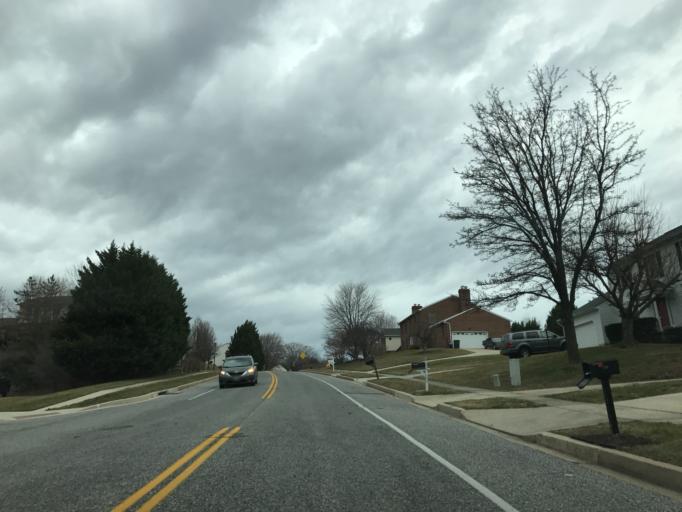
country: US
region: Maryland
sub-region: Harford County
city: South Bel Air
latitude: 39.5301
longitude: -76.3218
